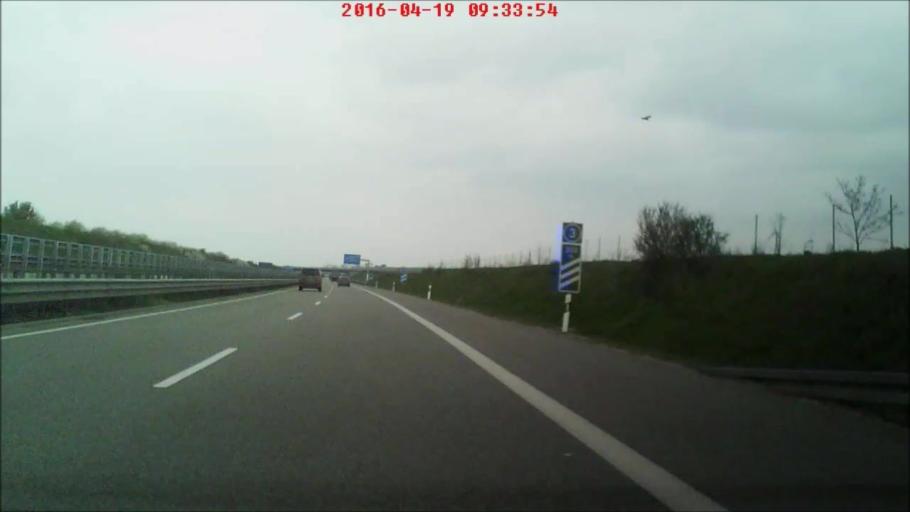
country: DE
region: Thuringia
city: Heldrungen
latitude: 51.2996
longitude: 11.2375
